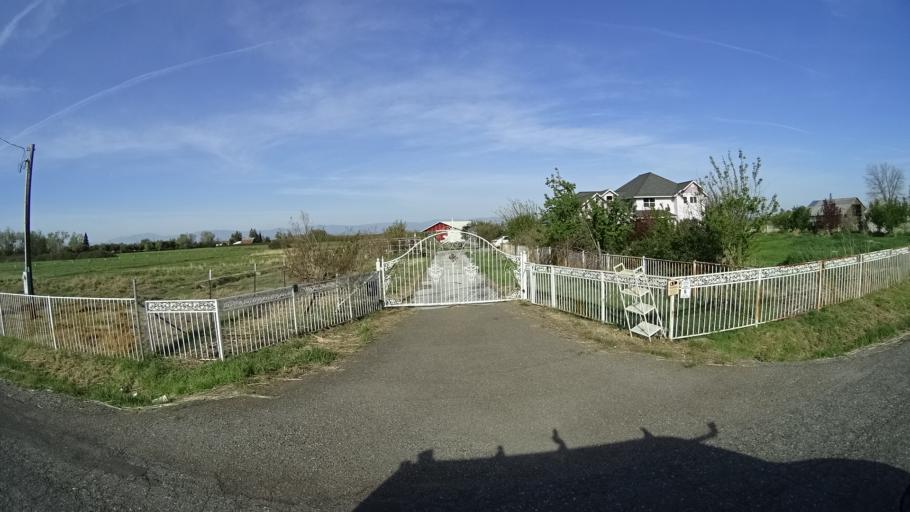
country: US
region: California
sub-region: Glenn County
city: Orland
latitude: 39.7210
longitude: -122.2158
